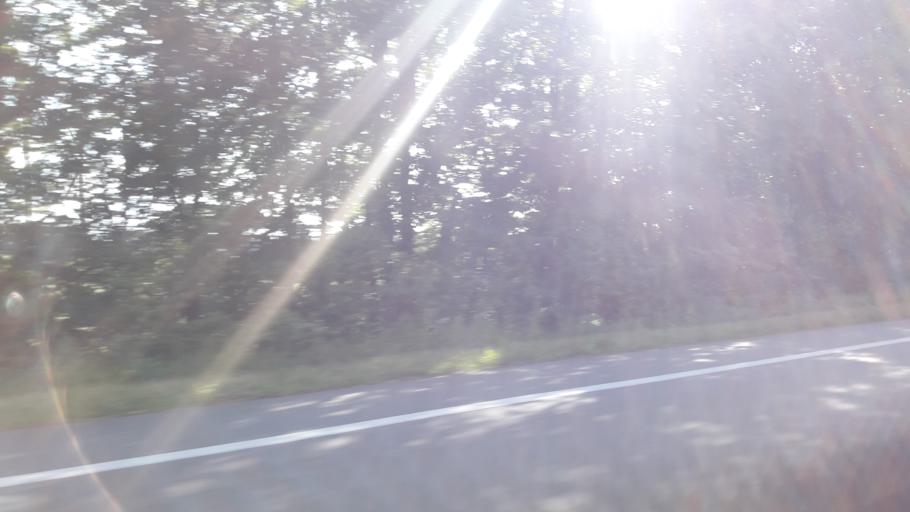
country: DE
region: North Rhine-Westphalia
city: Lichtenau
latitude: 51.6691
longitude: 8.8548
